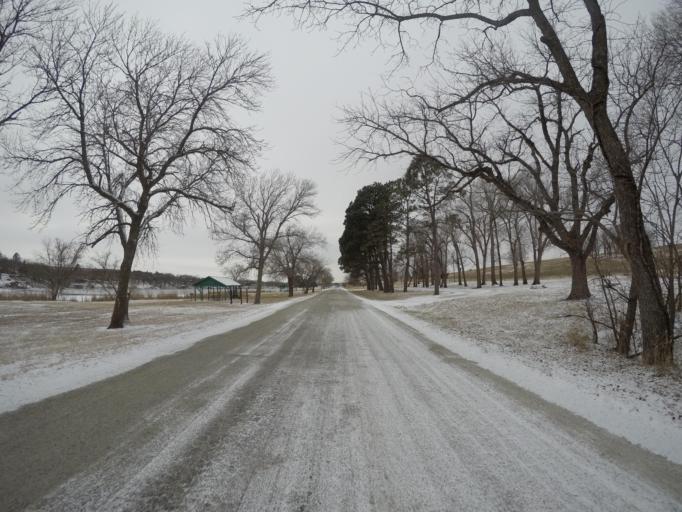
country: US
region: Kansas
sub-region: Wabaunsee County
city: Alma
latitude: 38.8638
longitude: -96.1806
